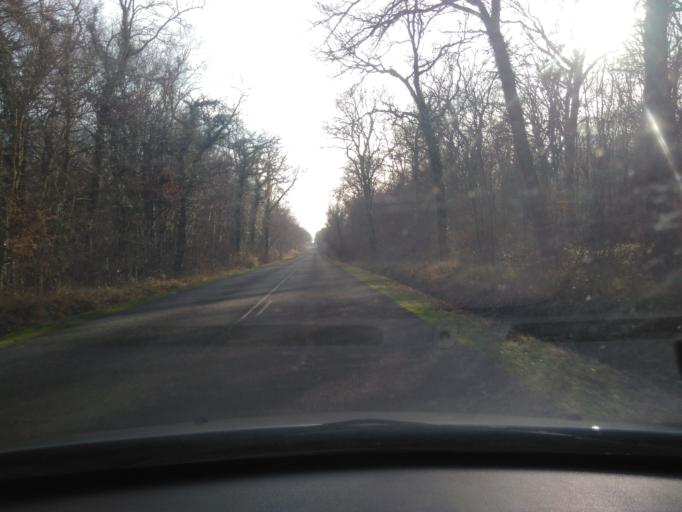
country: FR
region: Bourgogne
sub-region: Departement de la Nievre
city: Saint-Parize-le-Chatel
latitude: 46.8099
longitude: 3.2646
